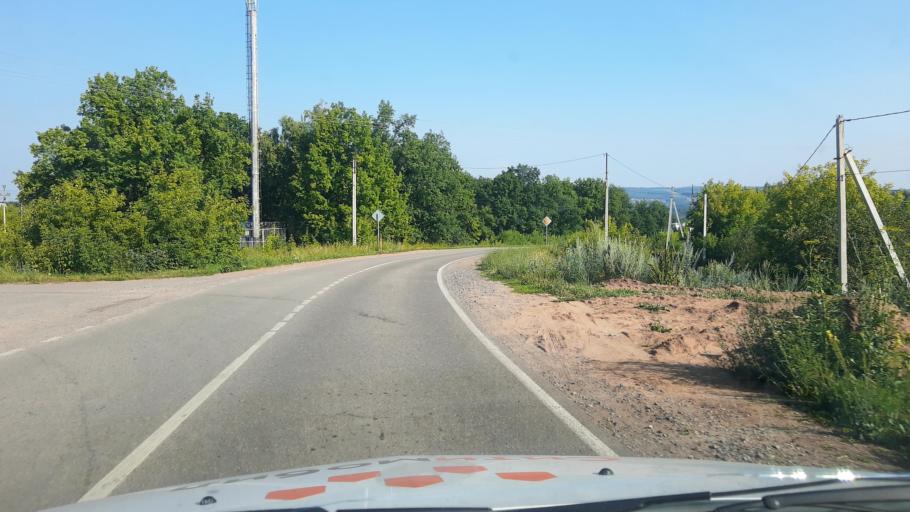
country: RU
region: Bashkortostan
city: Avdon
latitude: 54.6184
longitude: 55.6374
